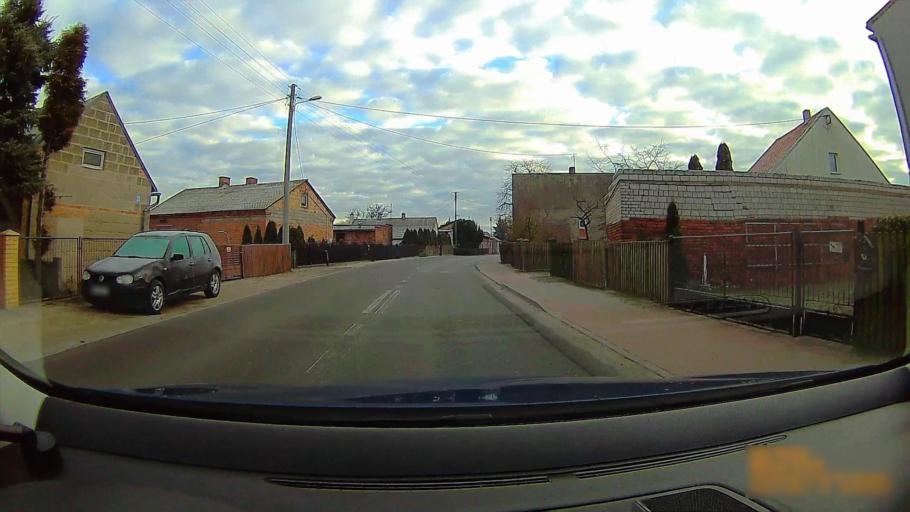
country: PL
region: Greater Poland Voivodeship
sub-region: Powiat koninski
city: Golina
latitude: 52.1943
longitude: 18.1239
